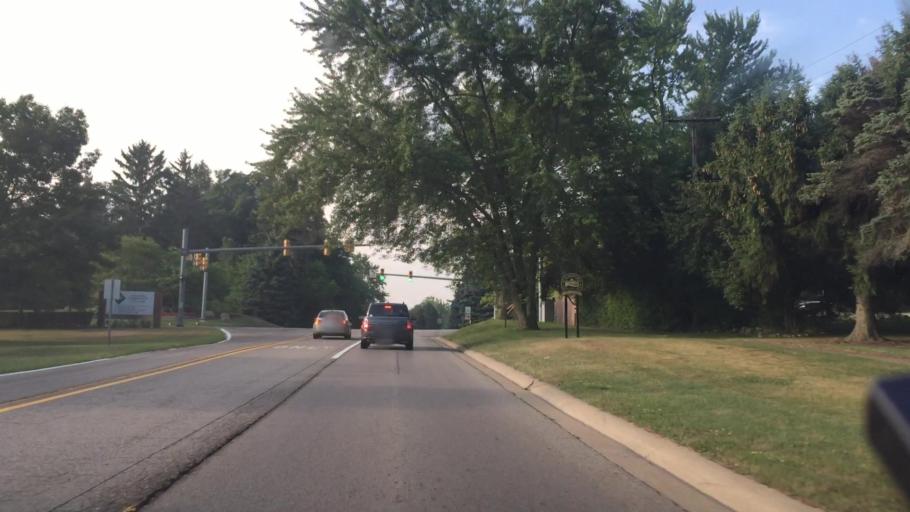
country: US
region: Michigan
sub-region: Oakland County
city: Bloomfield Hills
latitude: 42.5970
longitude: -83.2477
